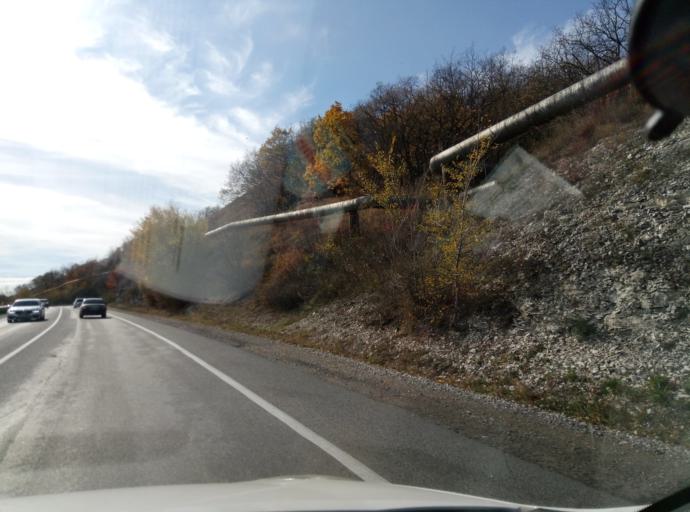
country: RU
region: Stavropol'skiy
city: Yasnaya Polyana
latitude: 43.9857
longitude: 42.7932
